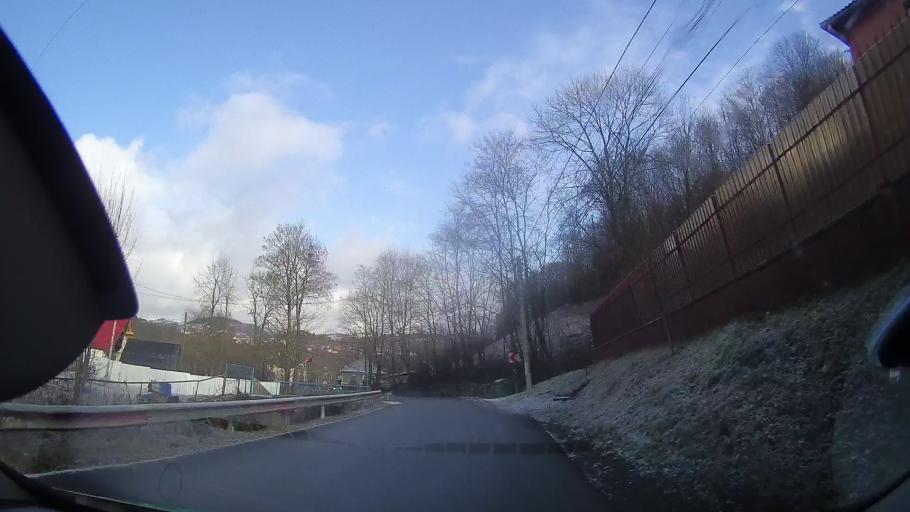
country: RO
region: Alba
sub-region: Comuna Sohodol
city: Sohodol
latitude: 46.3522
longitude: 23.0290
